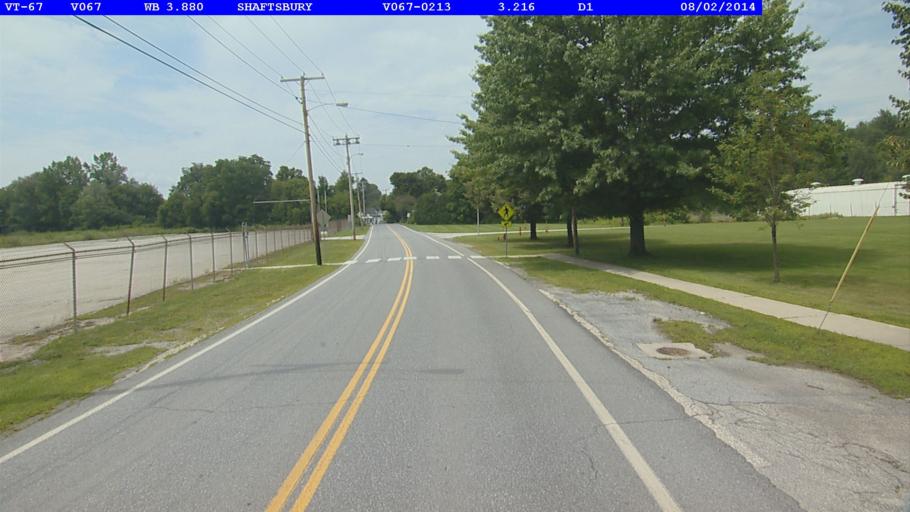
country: US
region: Vermont
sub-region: Bennington County
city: North Bennington
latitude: 42.9465
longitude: -73.2171
